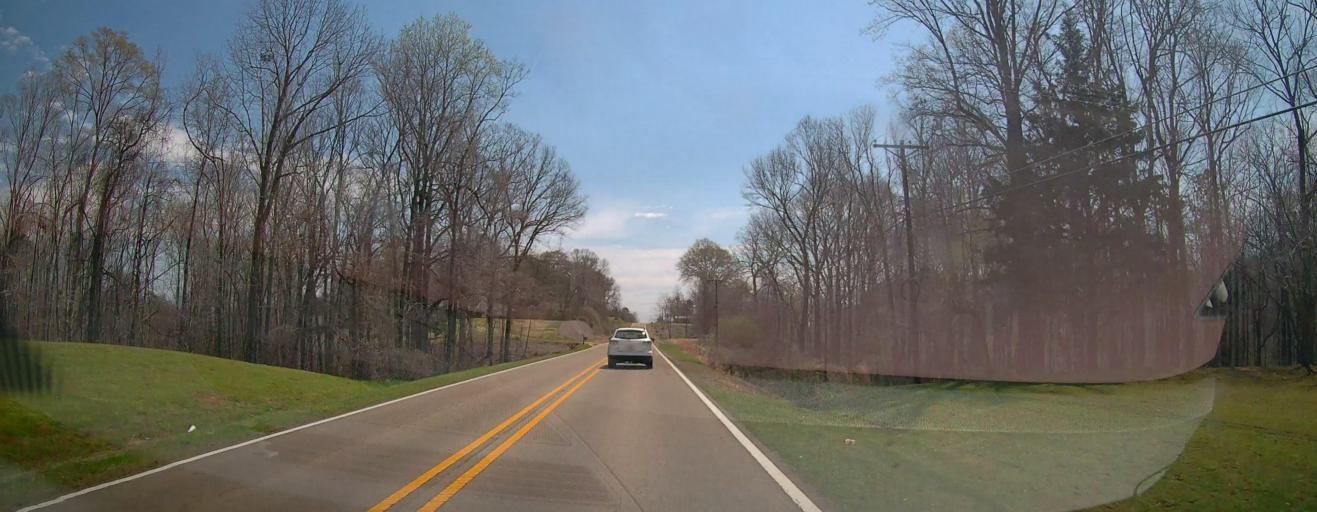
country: US
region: Mississippi
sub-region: Union County
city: New Albany
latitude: 34.4399
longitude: -88.9604
